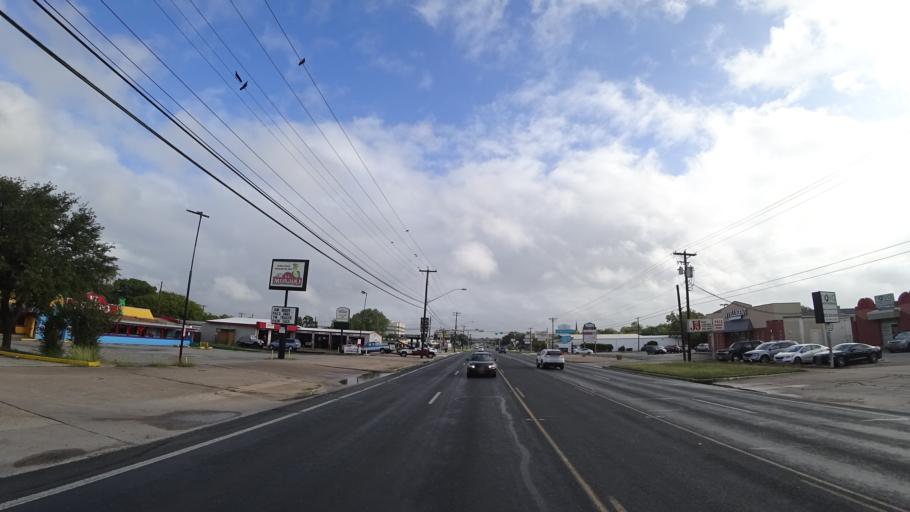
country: US
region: Texas
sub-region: Travis County
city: Austin
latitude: 30.3497
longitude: -97.7349
